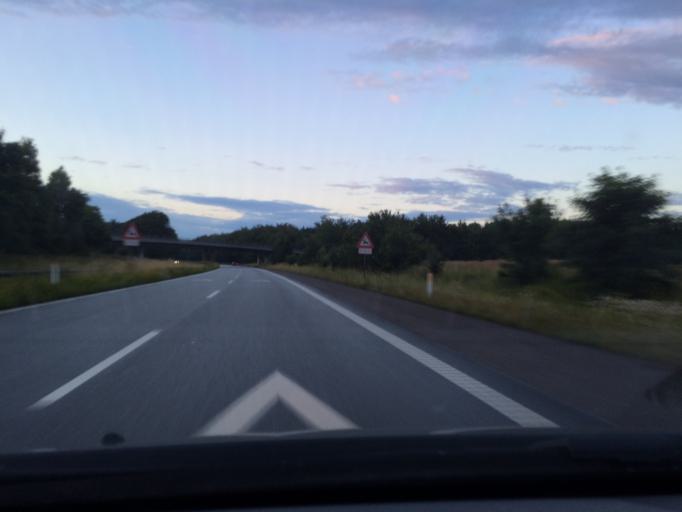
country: DK
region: Zealand
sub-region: Koge Kommune
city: Ejby
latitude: 55.4261
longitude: 12.1125
